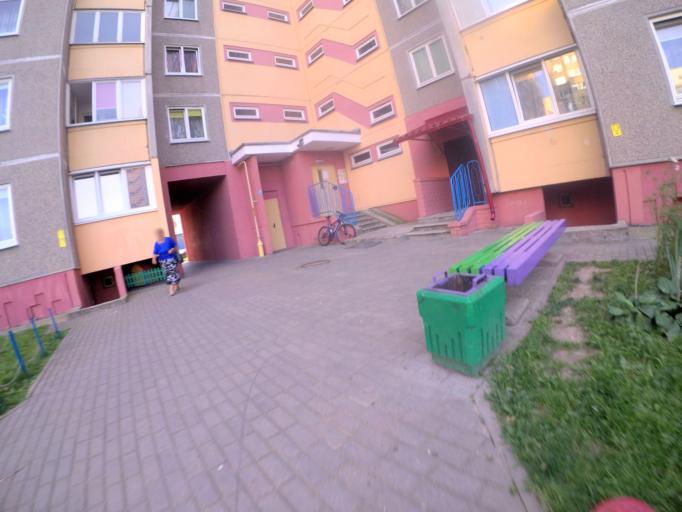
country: BY
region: Grodnenskaya
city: Hrodna
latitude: 53.6974
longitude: 23.8346
